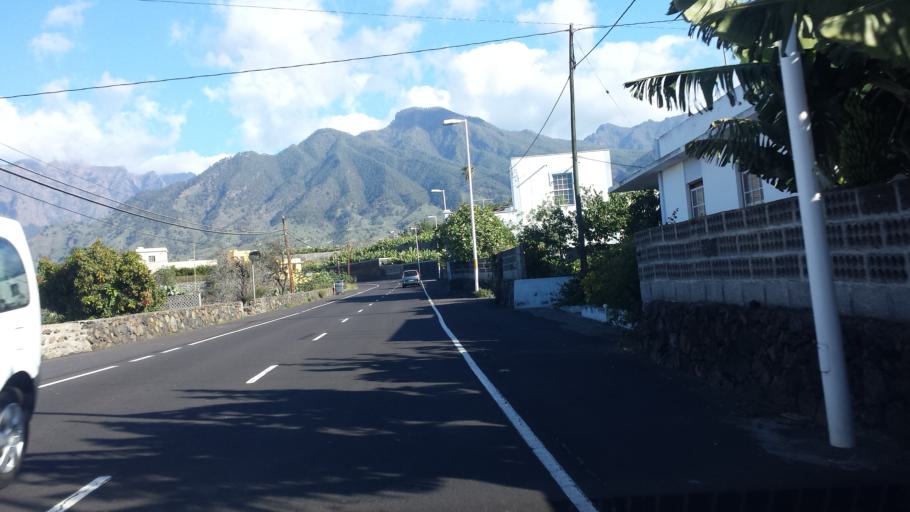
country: ES
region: Canary Islands
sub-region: Provincia de Santa Cruz de Tenerife
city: Los Llanos de Aridane
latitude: 28.6361
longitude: -17.9081
